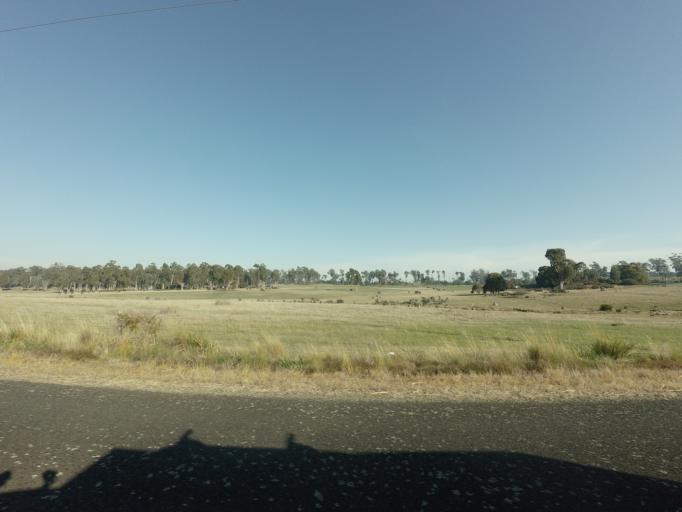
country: AU
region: Tasmania
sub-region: Northern Midlands
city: Longford
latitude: -41.5449
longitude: 146.9919
